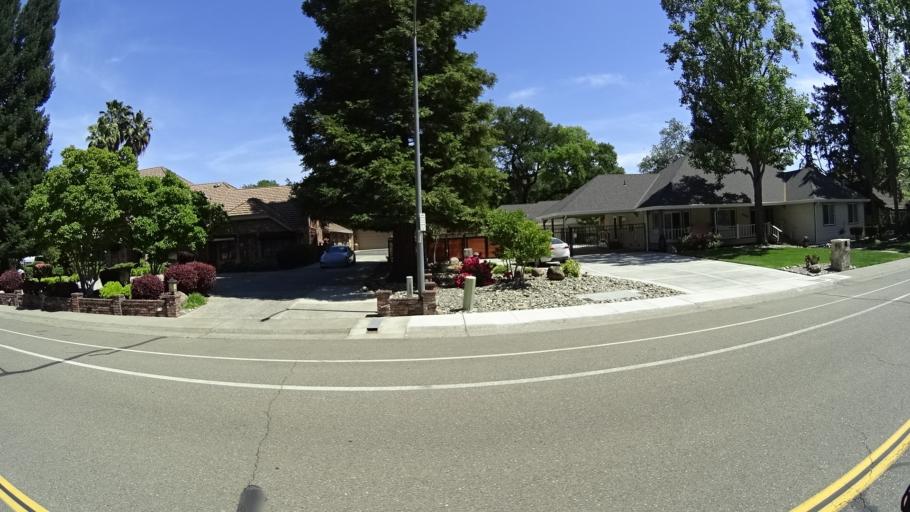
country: US
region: California
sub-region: Placer County
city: Rocklin
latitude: 38.8119
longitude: -121.2391
